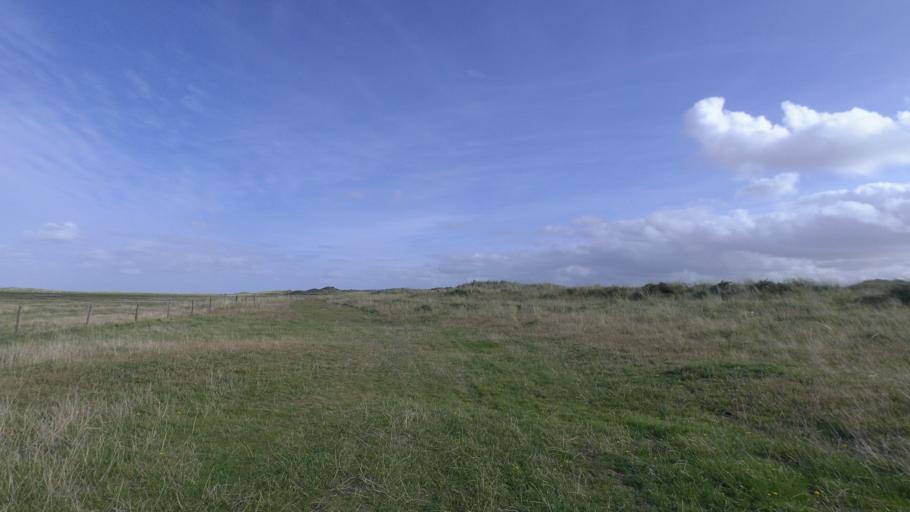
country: NL
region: Friesland
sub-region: Gemeente Ameland
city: Nes
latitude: 53.4517
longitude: 5.8517
